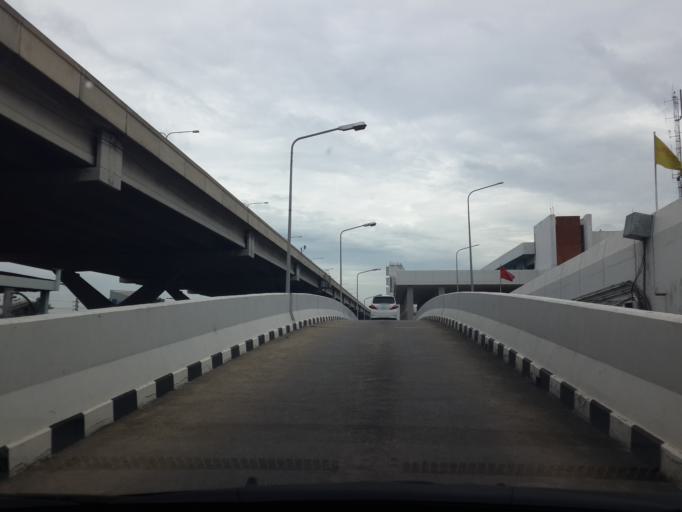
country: TH
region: Bangkok
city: Don Mueang
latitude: 13.9221
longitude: 100.6029
